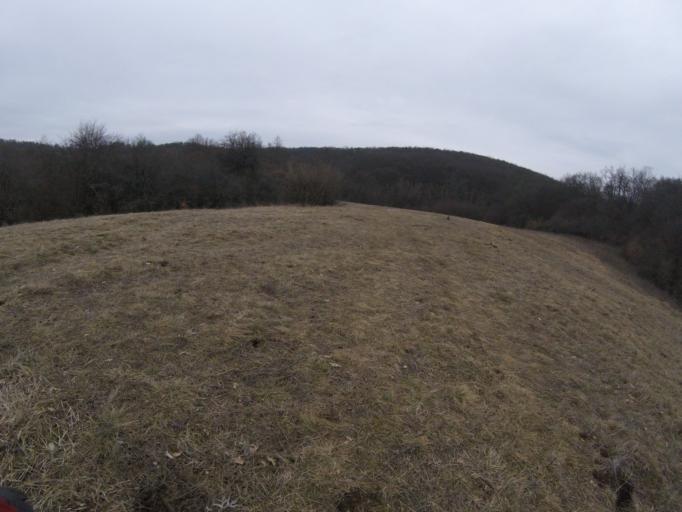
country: HU
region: Borsod-Abauj-Zemplen
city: Rudabanya
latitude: 48.4583
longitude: 20.6078
